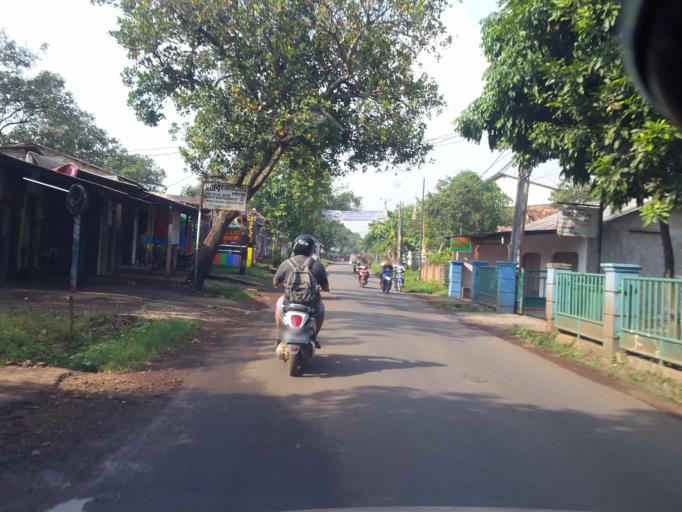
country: ID
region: West Java
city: Cileungsir
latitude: -6.3808
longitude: 106.9915
